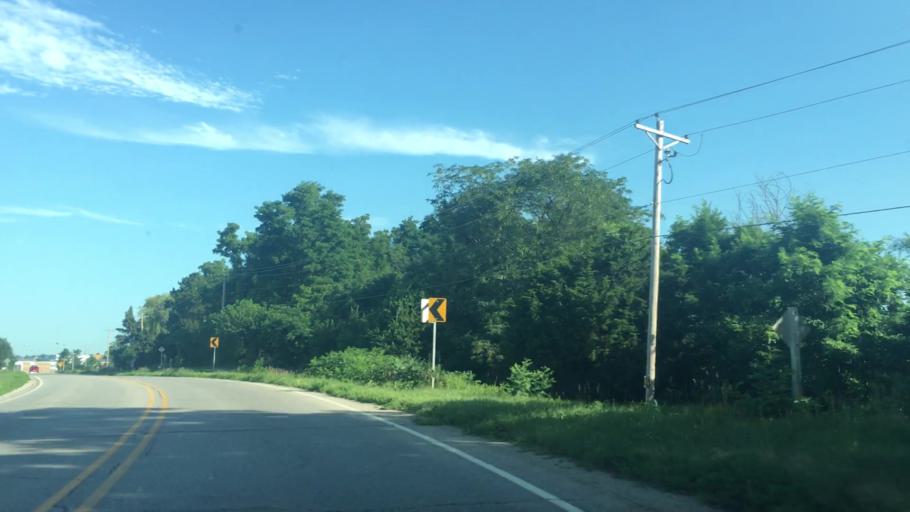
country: US
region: Iowa
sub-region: Johnson County
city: North Liberty
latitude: 41.7303
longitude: -91.5617
